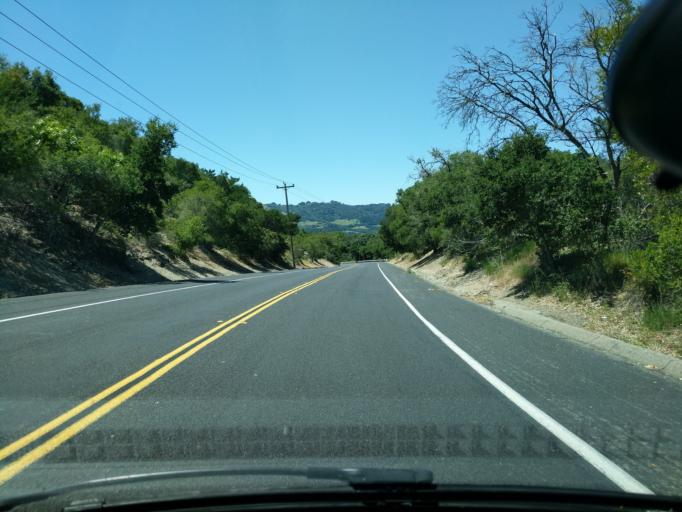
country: US
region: California
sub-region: Contra Costa County
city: Orinda
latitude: 37.9190
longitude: -122.1981
